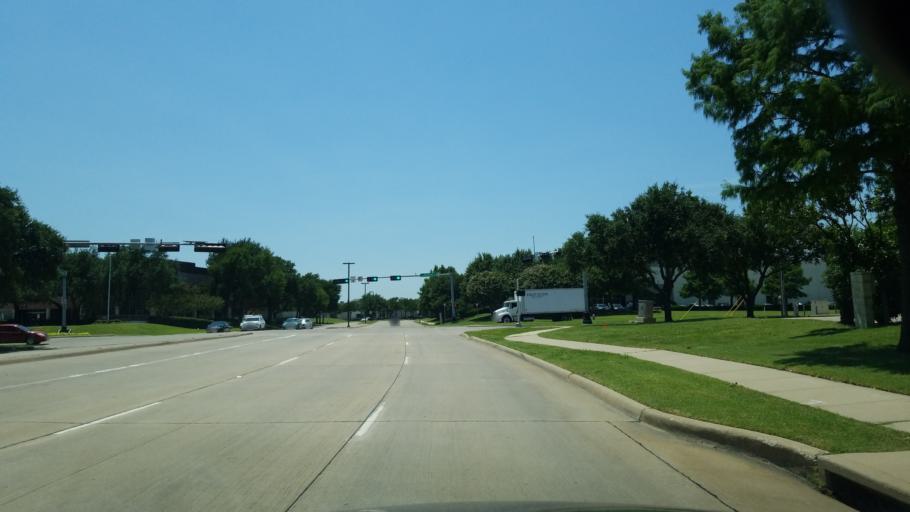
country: US
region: Texas
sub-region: Dallas County
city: Farmers Branch
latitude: 32.9392
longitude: -96.9153
